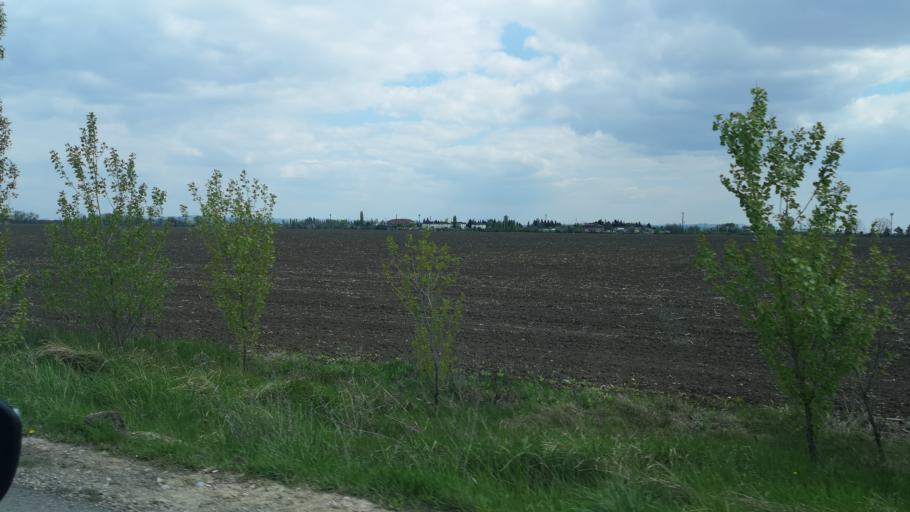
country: RO
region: Prahova
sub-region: Comuna Barcanesti
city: Tatarani
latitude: 44.8947
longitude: 26.0063
